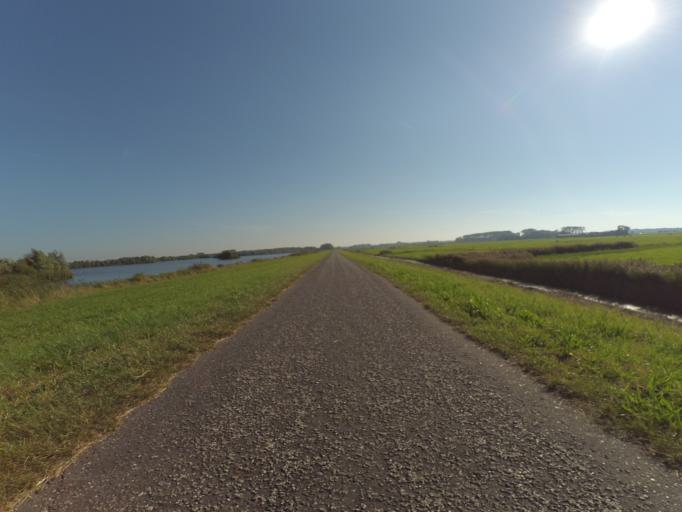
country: NL
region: Gelderland
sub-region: Gemeente Nijkerk
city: Nijkerk
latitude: 52.2639
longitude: 5.5123
